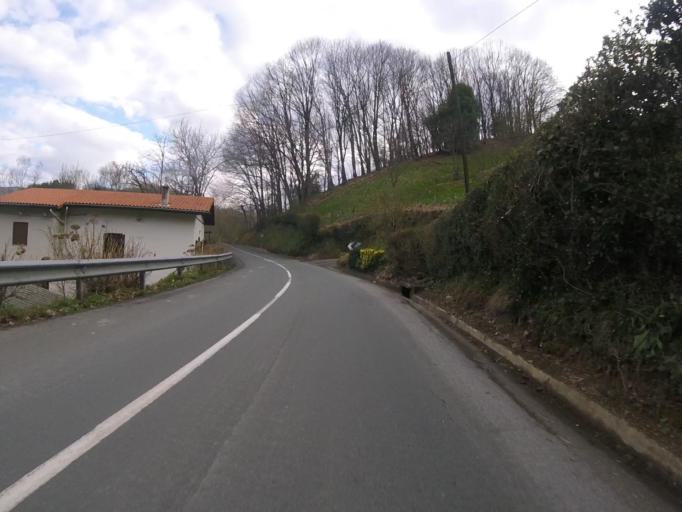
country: ES
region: Basque Country
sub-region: Provincia de Guipuzcoa
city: Irun
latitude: 43.3183
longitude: -1.8194
